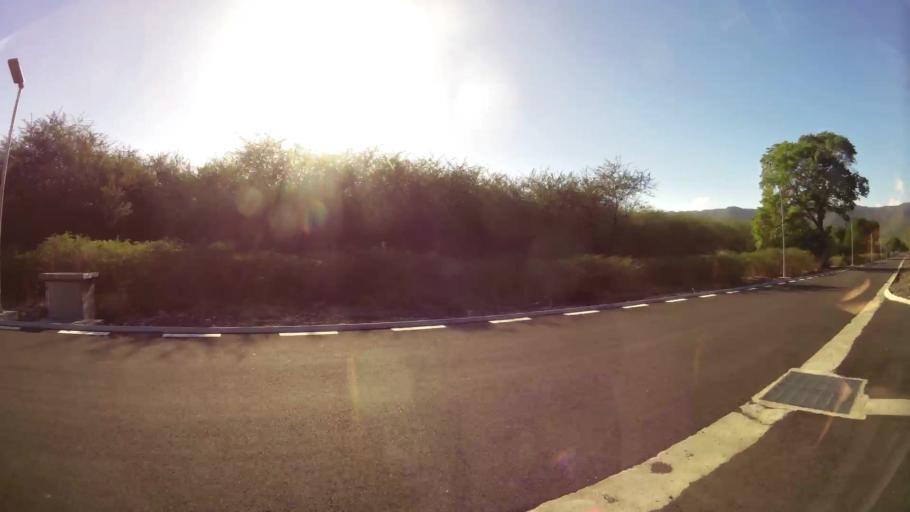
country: MU
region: Black River
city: Tamarin
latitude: -20.3443
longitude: 57.3919
